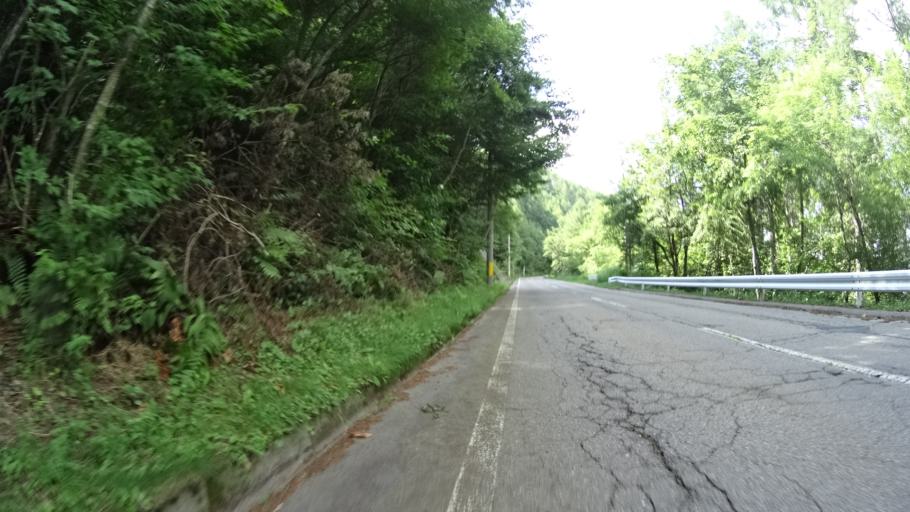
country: JP
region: Nagano
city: Saku
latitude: 36.0497
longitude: 138.4051
